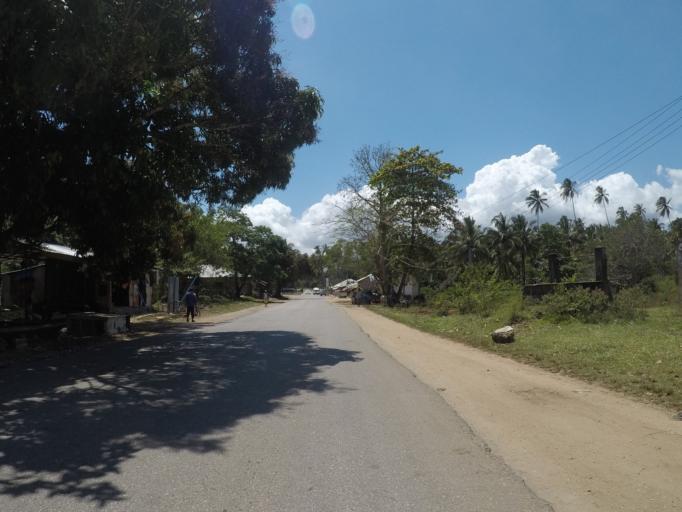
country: TZ
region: Zanzibar Central/South
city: Koani
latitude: -6.2054
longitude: 39.3252
